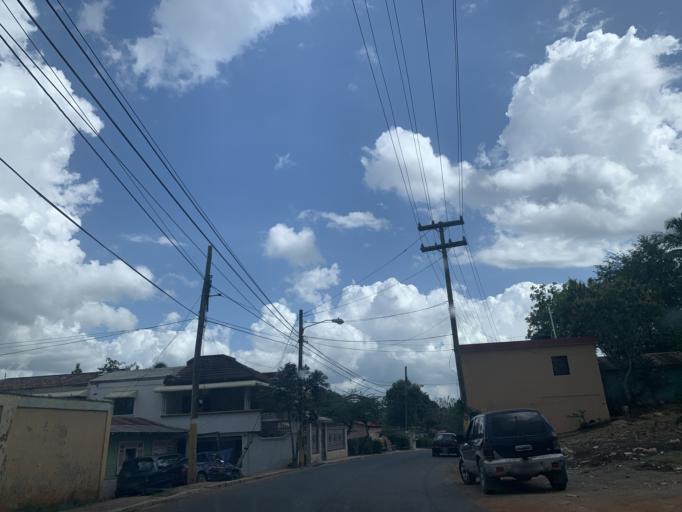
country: DO
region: Monte Plata
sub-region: Yamasa
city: Yamasa
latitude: 18.7725
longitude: -70.0203
